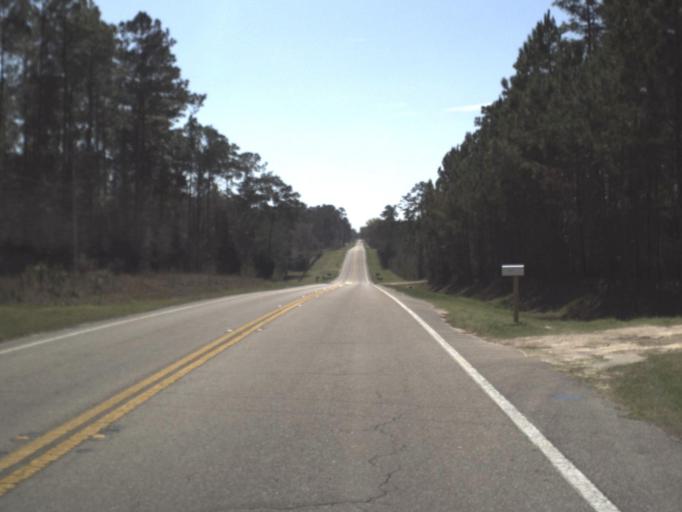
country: US
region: Florida
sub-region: Jefferson County
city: Monticello
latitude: 30.3978
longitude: -84.0167
